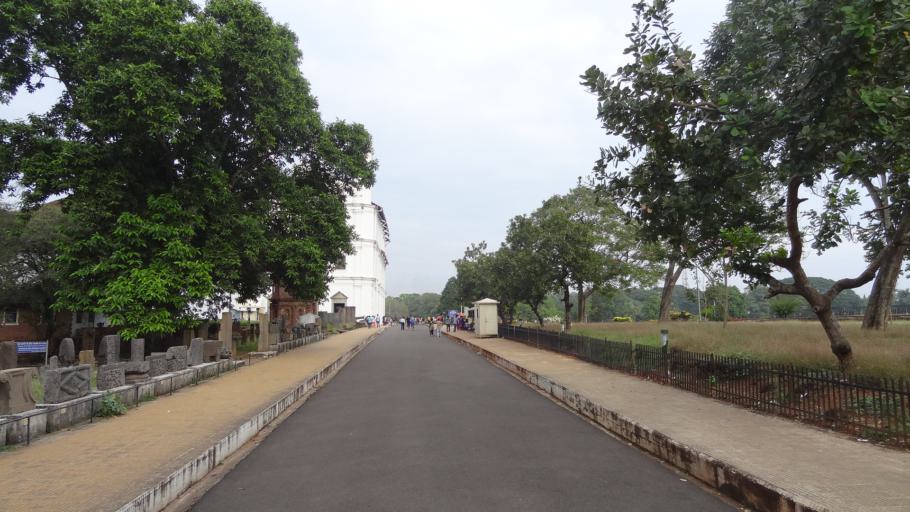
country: IN
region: Goa
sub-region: North Goa
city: Jua
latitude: 15.5027
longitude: 73.9102
